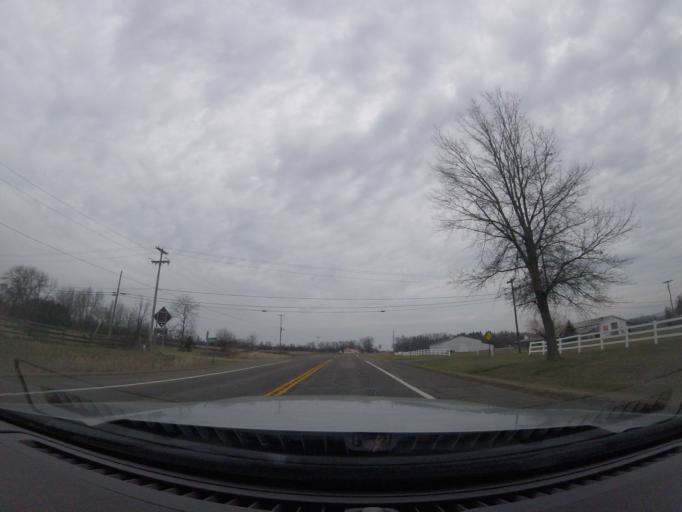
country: US
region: New York
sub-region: Yates County
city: Dundee
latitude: 42.5159
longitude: -76.9227
